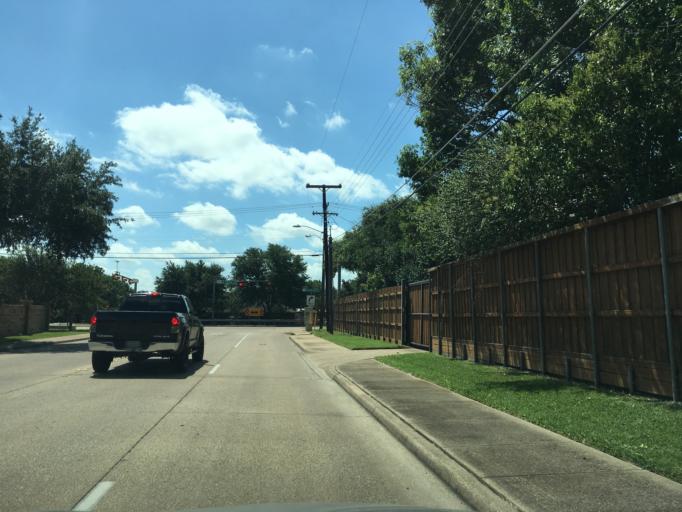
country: US
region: Texas
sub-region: Dallas County
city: Garland
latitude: 32.8374
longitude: -96.6479
